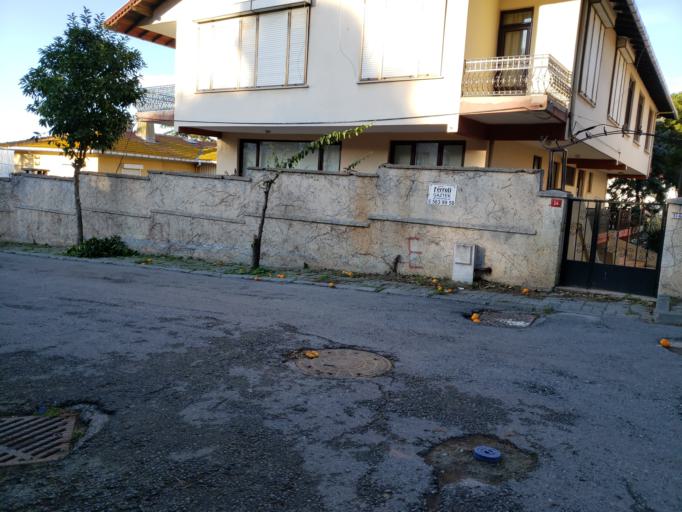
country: TR
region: Istanbul
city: Adalan
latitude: 40.8794
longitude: 29.0913
